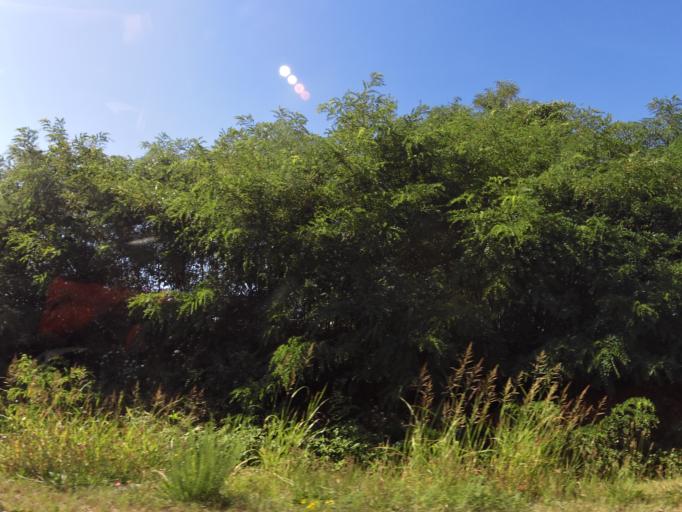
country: US
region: Arkansas
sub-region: Clay County
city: Piggott
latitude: 36.4289
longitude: -90.2474
